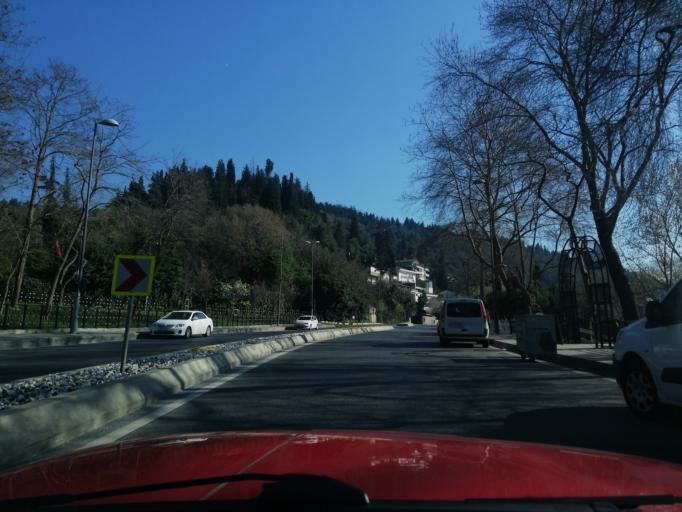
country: TR
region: Istanbul
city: UEskuedar
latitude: 41.0685
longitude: 29.0576
